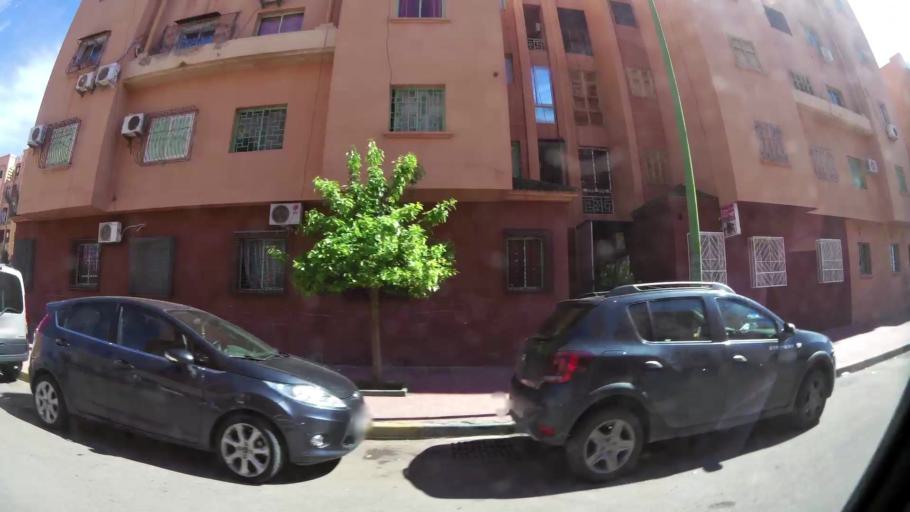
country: MA
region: Marrakech-Tensift-Al Haouz
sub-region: Marrakech
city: Marrakesh
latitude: 31.6744
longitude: -8.0174
